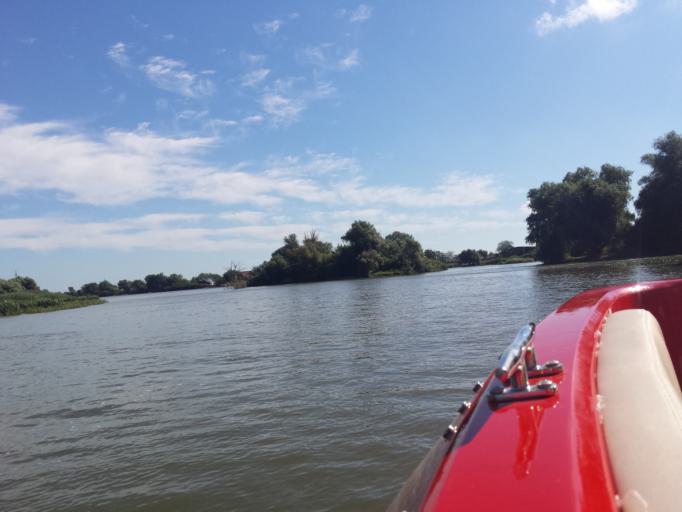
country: RO
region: Tulcea
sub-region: Comuna Crisan
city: Crisan
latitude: 45.2177
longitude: 29.2288
